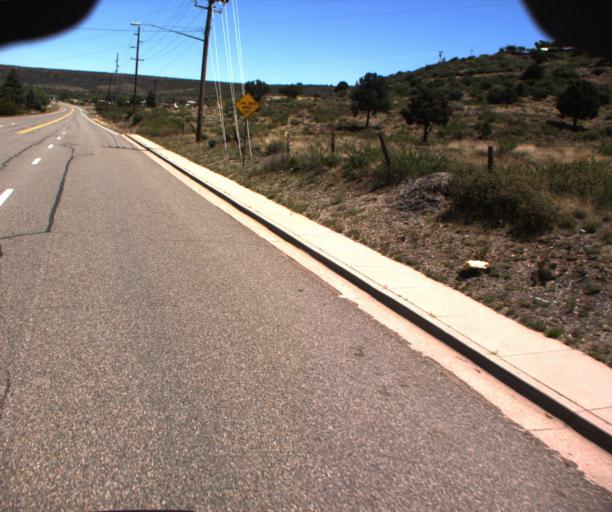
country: US
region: Arizona
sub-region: Yavapai County
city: Congress
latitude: 34.2260
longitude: -112.7435
